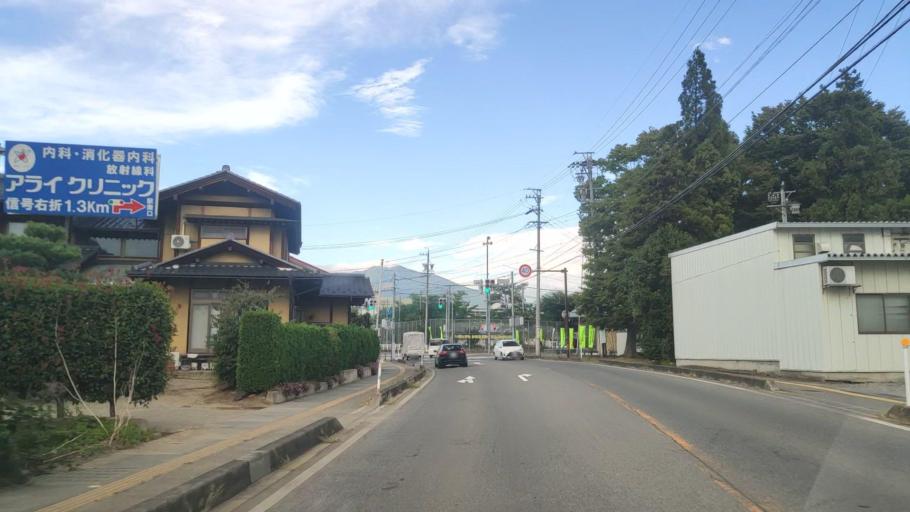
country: JP
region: Nagano
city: Nakano
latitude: 36.7417
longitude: 138.3493
